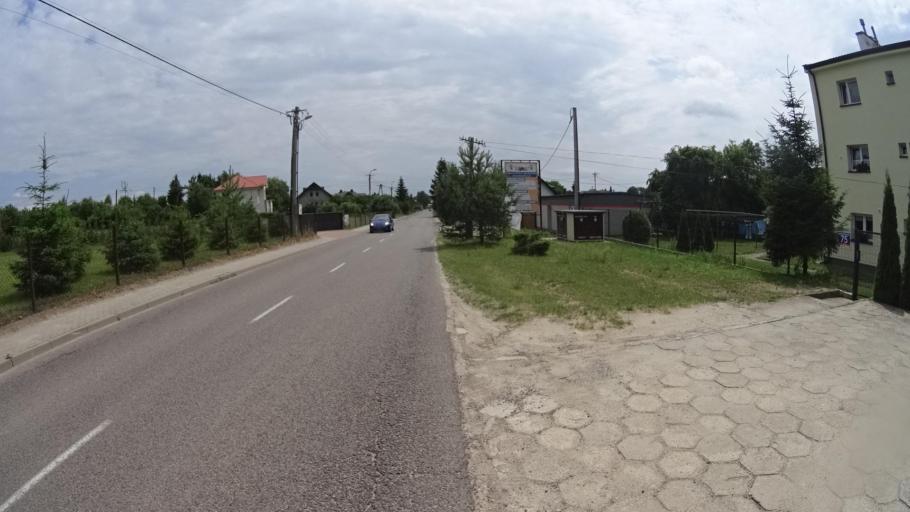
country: PL
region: Masovian Voivodeship
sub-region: Powiat piaseczynski
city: Tarczyn
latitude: 51.9874
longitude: 20.8262
